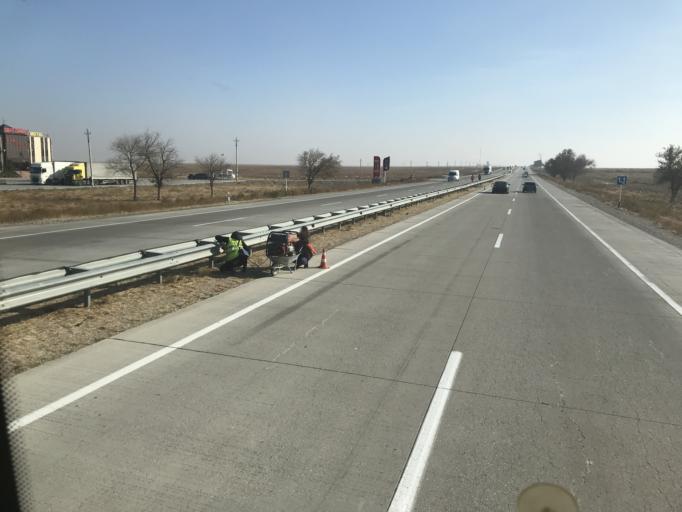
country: KZ
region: Ongtustik Qazaqstan
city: Temirlanovka
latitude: 42.8407
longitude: 69.1055
